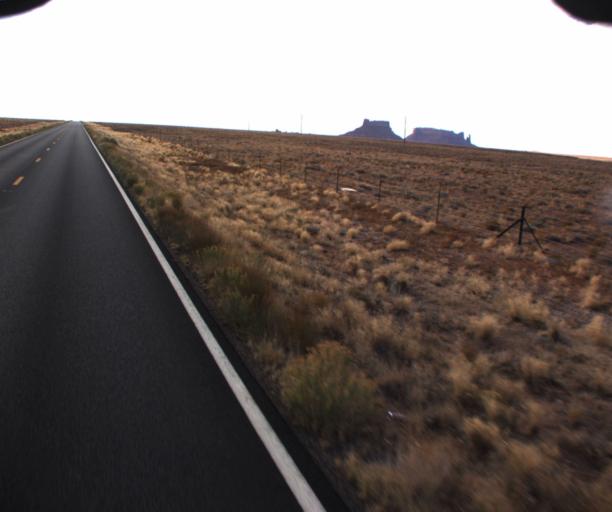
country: US
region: Arizona
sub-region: Apache County
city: Many Farms
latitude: 36.5753
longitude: -109.5509
